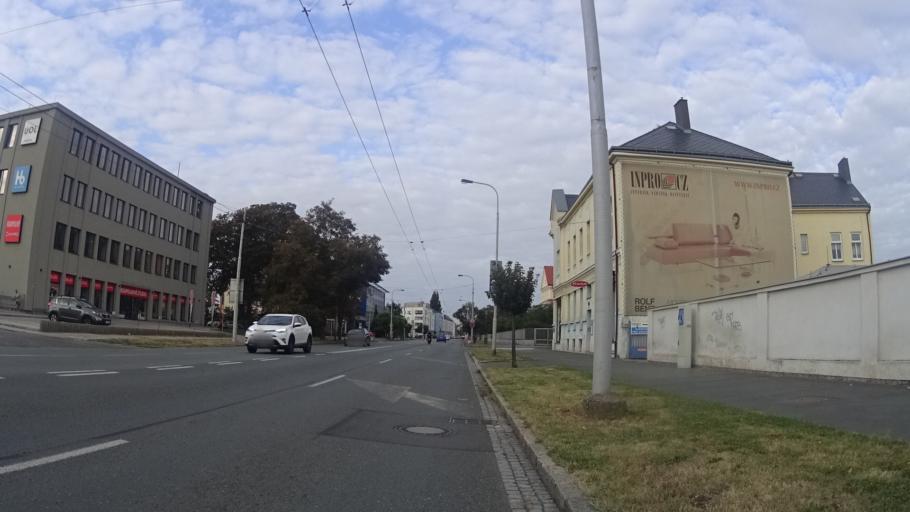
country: CZ
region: Kralovehradecky
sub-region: Okres Hradec Kralove
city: Hradec Kralove
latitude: 50.2093
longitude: 15.8039
